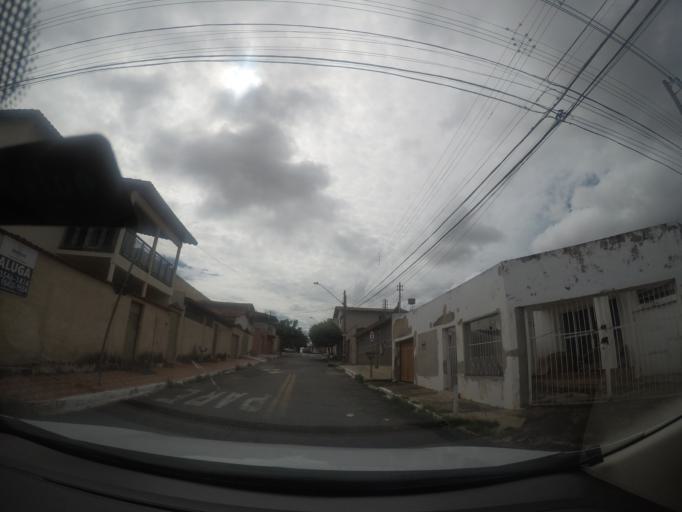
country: BR
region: Goias
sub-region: Goiania
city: Goiania
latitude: -16.6663
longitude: -49.2957
